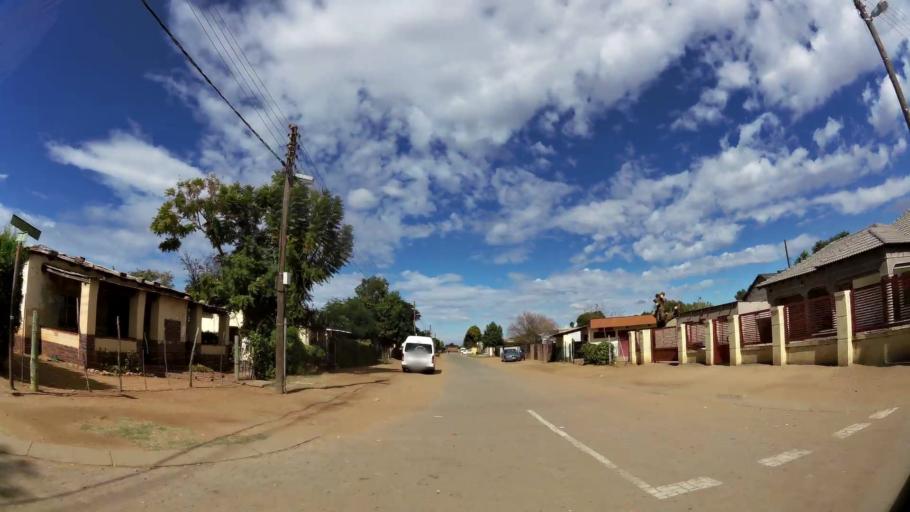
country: ZA
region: Limpopo
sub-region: Waterberg District Municipality
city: Bela-Bela
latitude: -24.8880
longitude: 28.3156
